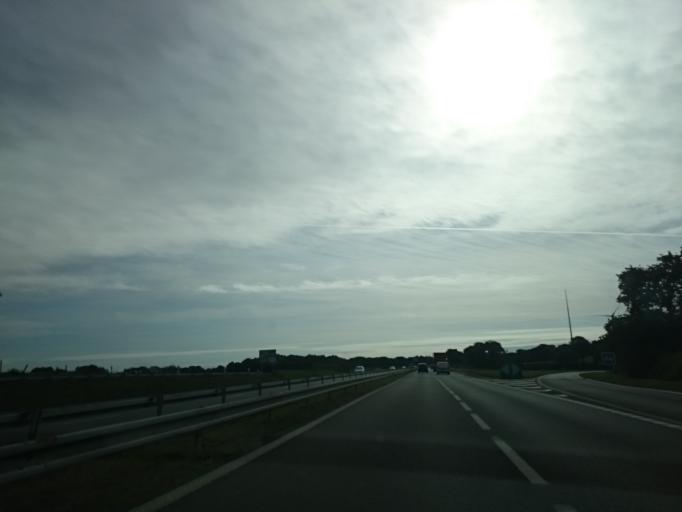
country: FR
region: Brittany
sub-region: Departement du Morbihan
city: Ambon
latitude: 47.5903
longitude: -2.5534
